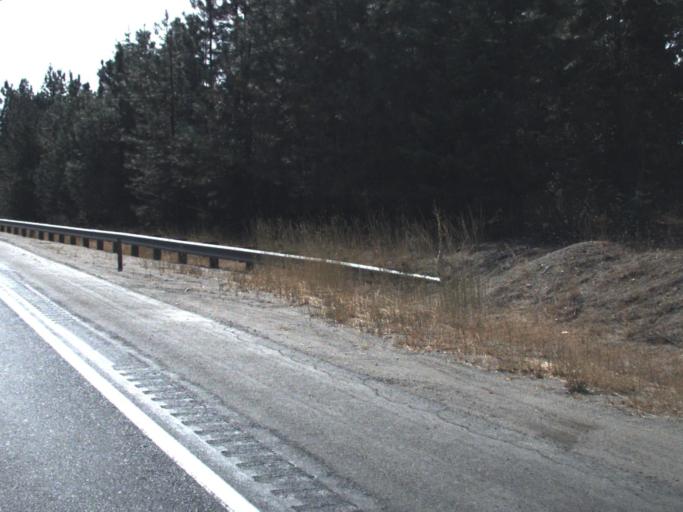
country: US
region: Washington
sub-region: Spokane County
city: Deer Park
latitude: 48.0362
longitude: -117.6051
